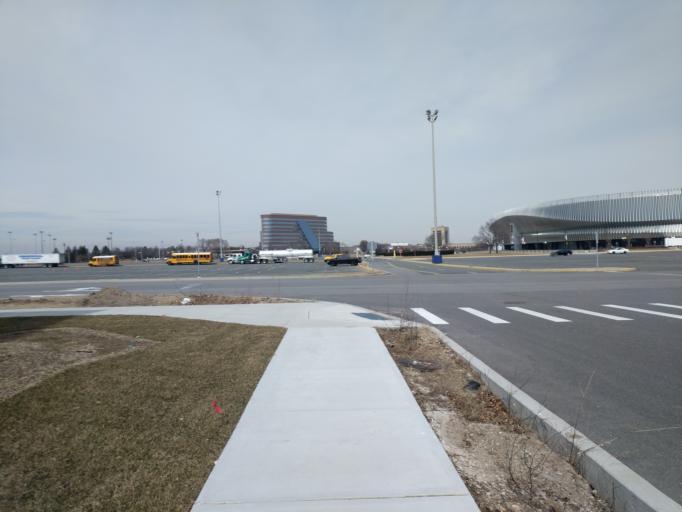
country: US
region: New York
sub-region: Nassau County
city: East Garden City
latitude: 40.7206
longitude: -73.5914
